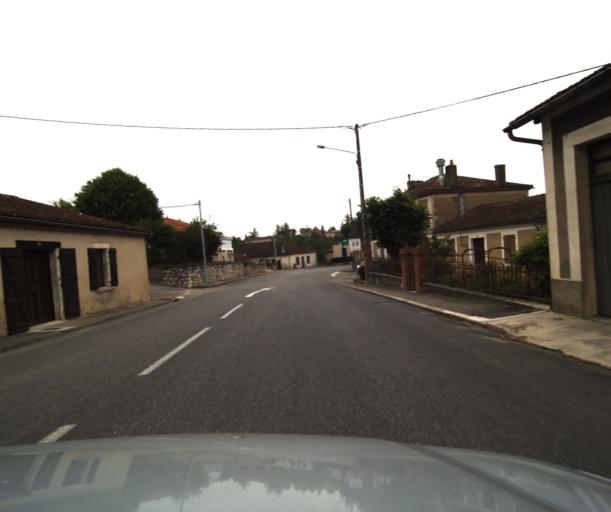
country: FR
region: Midi-Pyrenees
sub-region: Departement du Gers
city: Gimont
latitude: 43.7288
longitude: 0.8777
